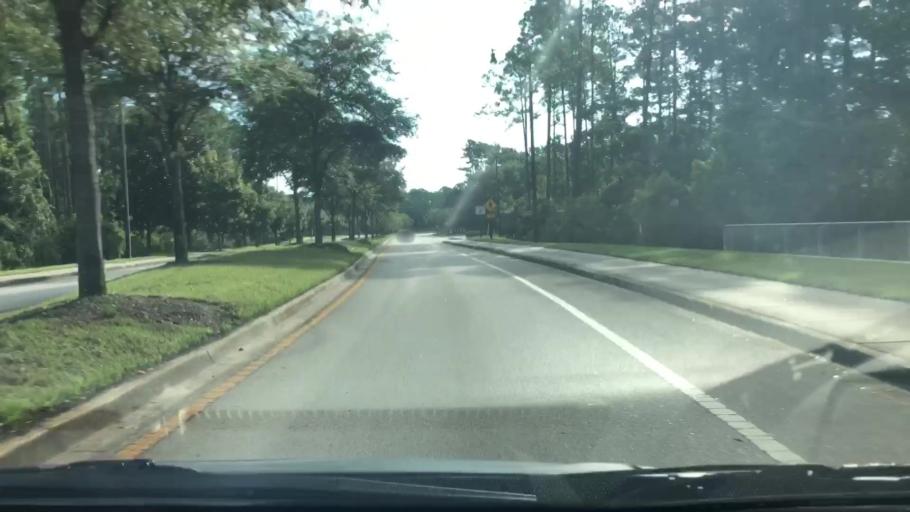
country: US
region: Florida
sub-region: Saint Johns County
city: Palm Valley
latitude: 30.1244
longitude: -81.4275
